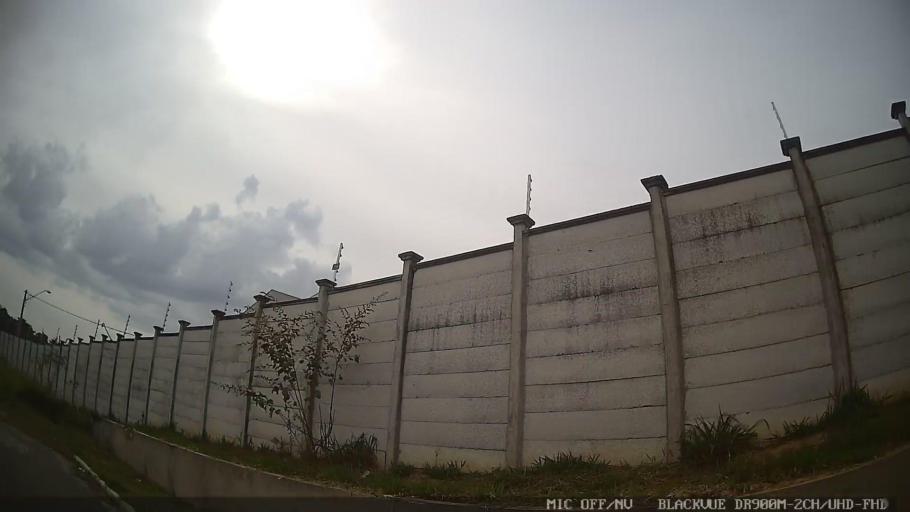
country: BR
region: Sao Paulo
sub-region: Indaiatuba
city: Indaiatuba
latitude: -23.0949
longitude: -47.2599
